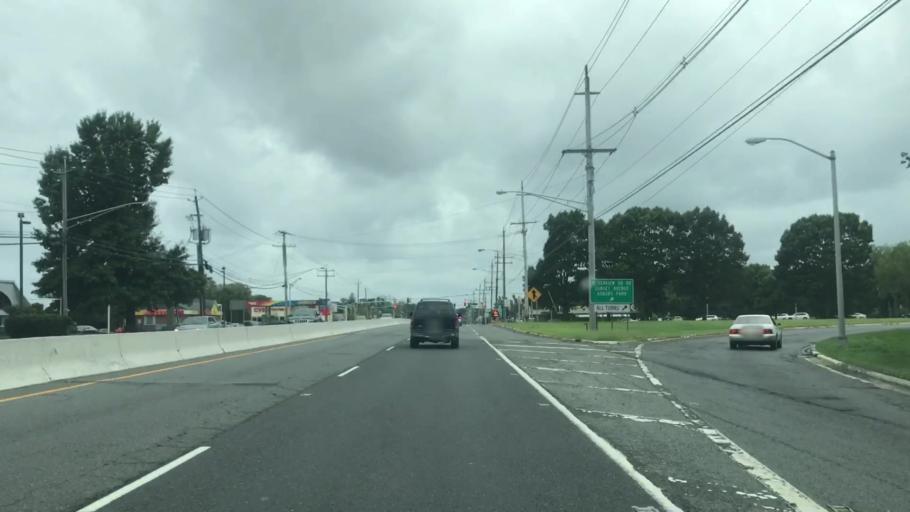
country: US
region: New Jersey
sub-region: Monmouth County
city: Wanamassa
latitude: 40.2374
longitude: -74.0377
